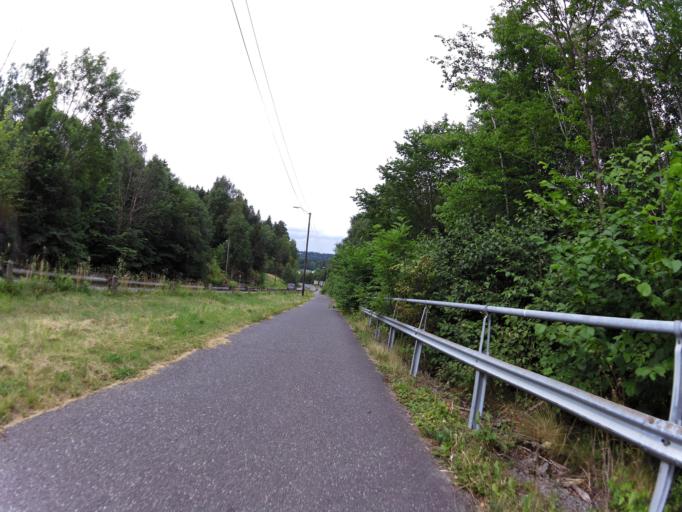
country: NO
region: Akershus
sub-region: As
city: As
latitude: 59.7368
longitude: 10.7541
